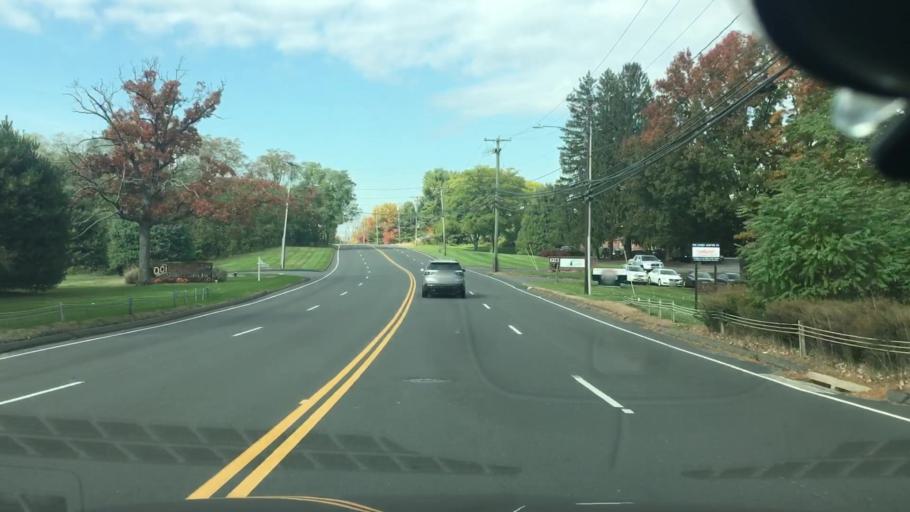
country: US
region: Connecticut
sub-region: Hartford County
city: Bristol
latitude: 41.6520
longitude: -72.9075
